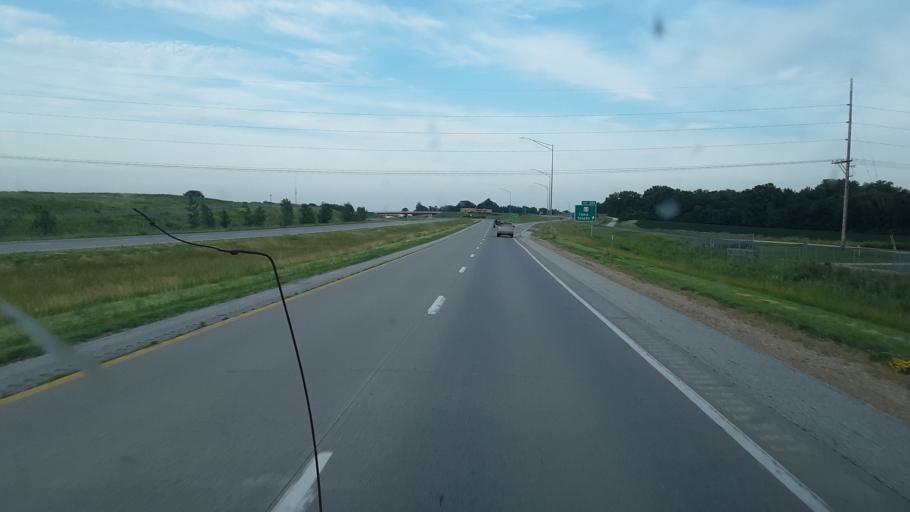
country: US
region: Iowa
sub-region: Tama County
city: Toledo
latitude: 41.9832
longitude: -92.5918
